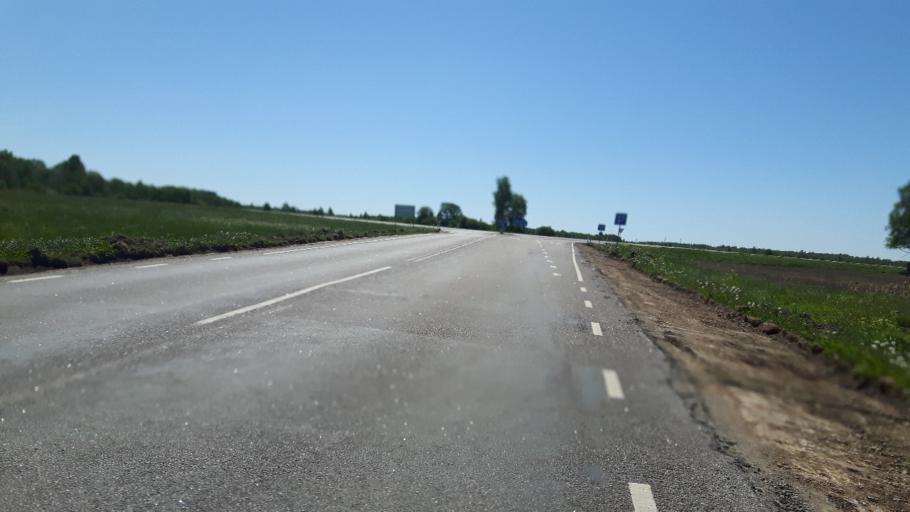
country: EE
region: Ida-Virumaa
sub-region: Narva-Joesuu linn
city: Narva-Joesuu
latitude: 59.3795
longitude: 27.9216
